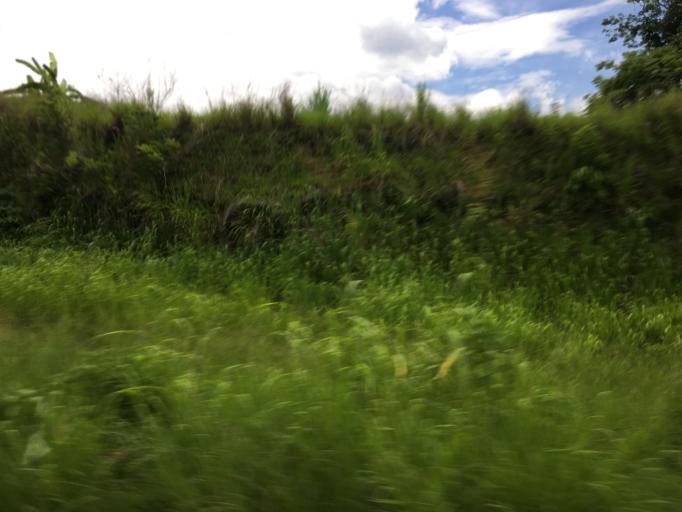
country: GT
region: Escuintla
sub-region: Municipio de Escuintla
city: Escuintla
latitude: 14.3452
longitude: -90.8036
